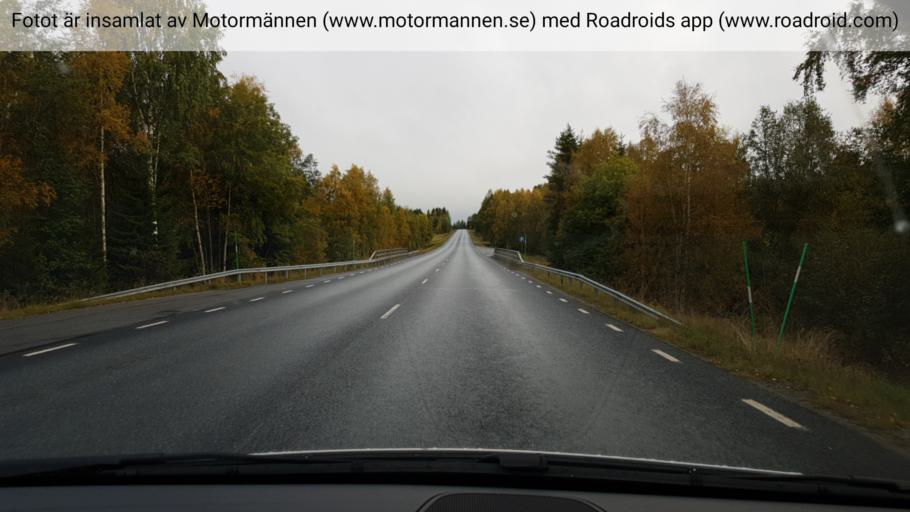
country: SE
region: Vaesterbotten
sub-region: Umea Kommun
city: Ersmark
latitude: 63.8877
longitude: 20.3087
